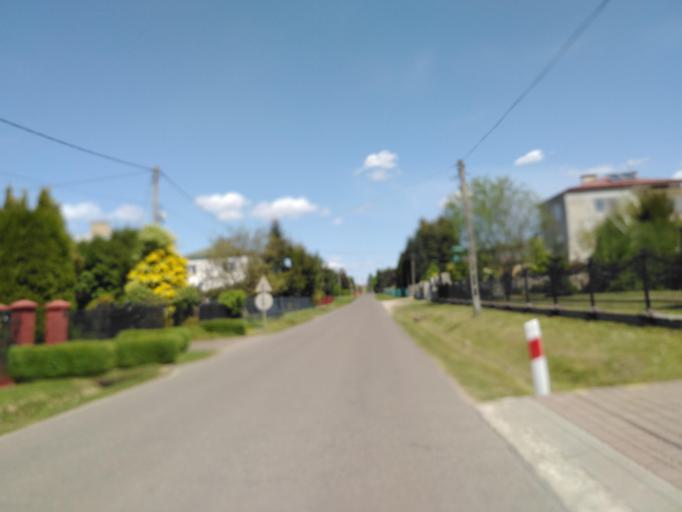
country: PL
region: Subcarpathian Voivodeship
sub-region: Powiat krosnienski
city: Jedlicze
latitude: 49.6991
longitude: 21.6806
